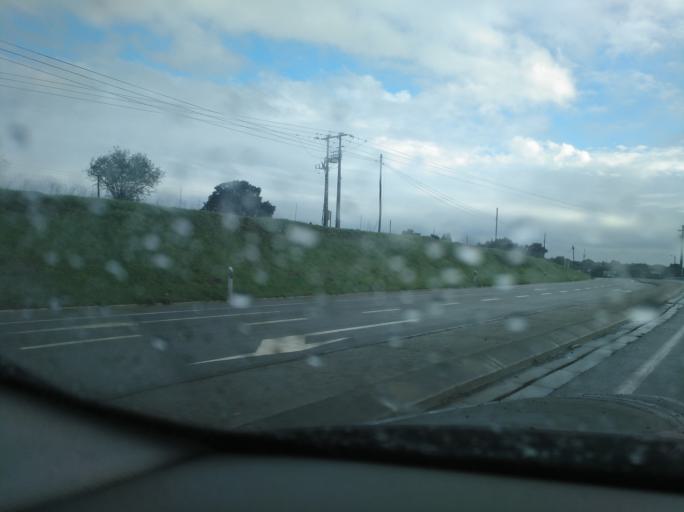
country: PT
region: Setubal
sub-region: Grandola
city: Grandola
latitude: 38.0732
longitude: -8.4163
